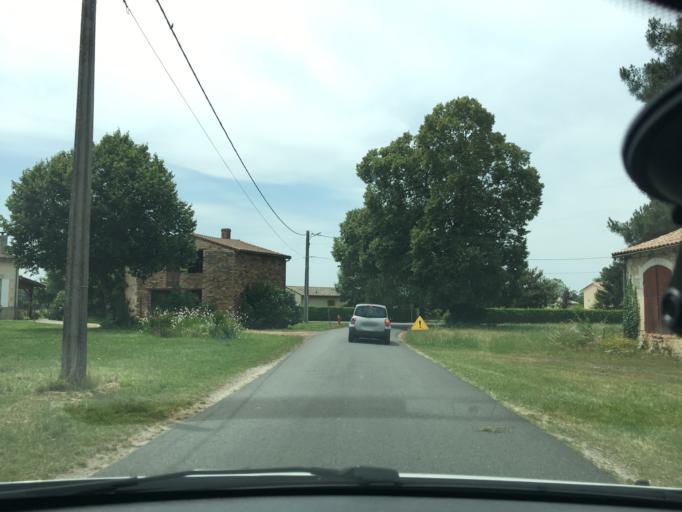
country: FR
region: Aquitaine
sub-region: Departement de la Gironde
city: Listrac-Medoc
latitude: 45.0632
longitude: -0.8002
